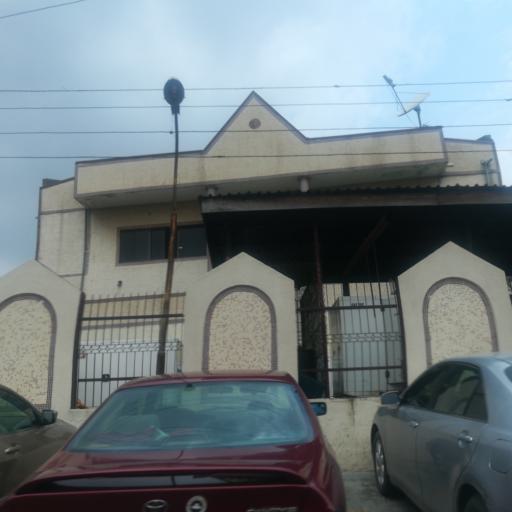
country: NG
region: Lagos
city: Ojota
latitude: 6.5753
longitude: 3.3901
